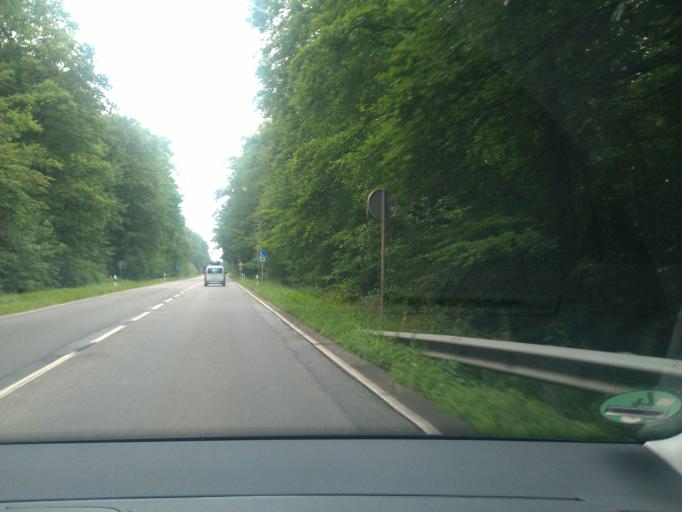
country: DE
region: North Rhine-Westphalia
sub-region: Regierungsbezirk Koln
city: Aachen
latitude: 50.7337
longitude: 6.1140
